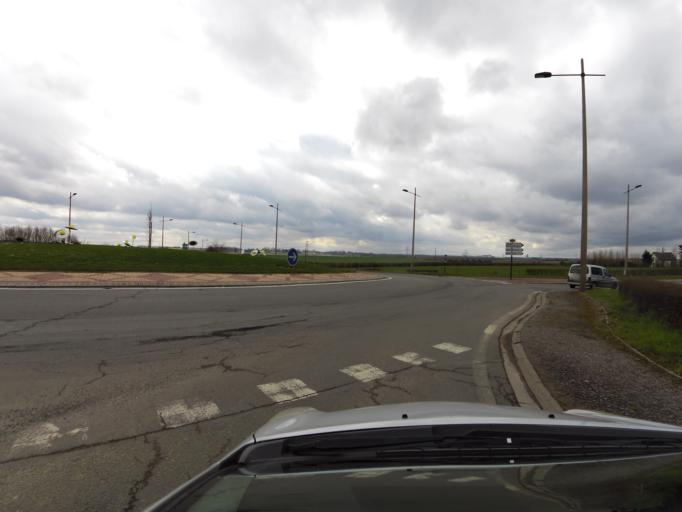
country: FR
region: Nord-Pas-de-Calais
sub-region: Departement du Pas-de-Calais
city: Beaurains
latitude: 50.2553
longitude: 2.7891
